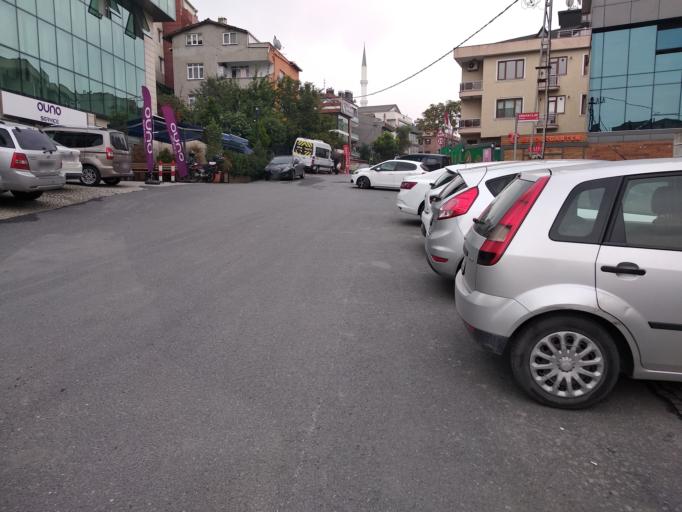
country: TR
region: Istanbul
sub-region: Atasehir
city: Atasehir
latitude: 40.9839
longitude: 29.1125
